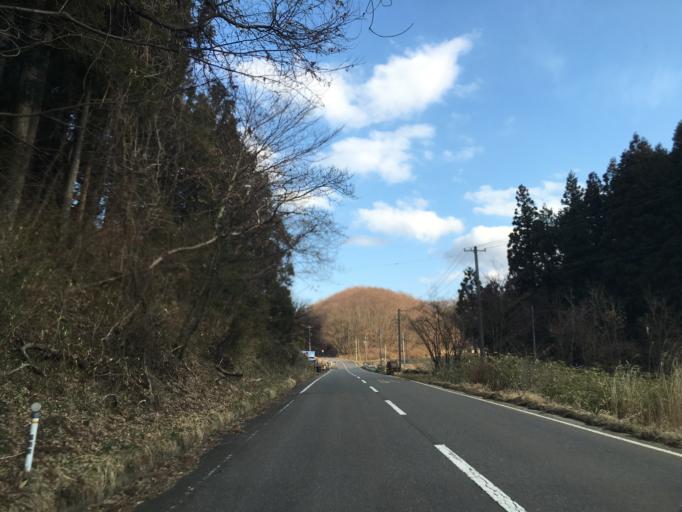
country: JP
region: Fukushima
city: Ishikawa
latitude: 37.1633
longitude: 140.5928
